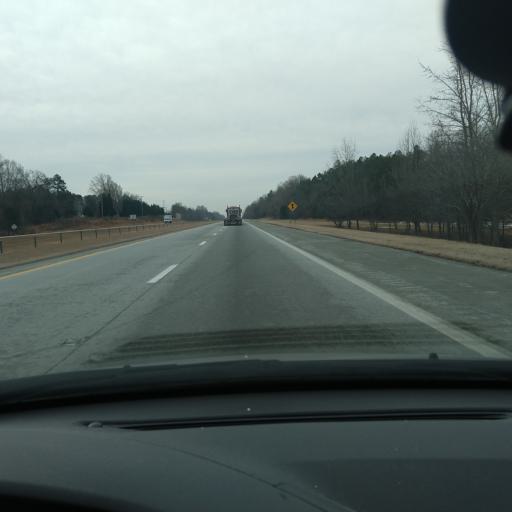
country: US
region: North Carolina
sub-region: Davidson County
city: Lexington
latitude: 35.8351
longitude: -80.2829
